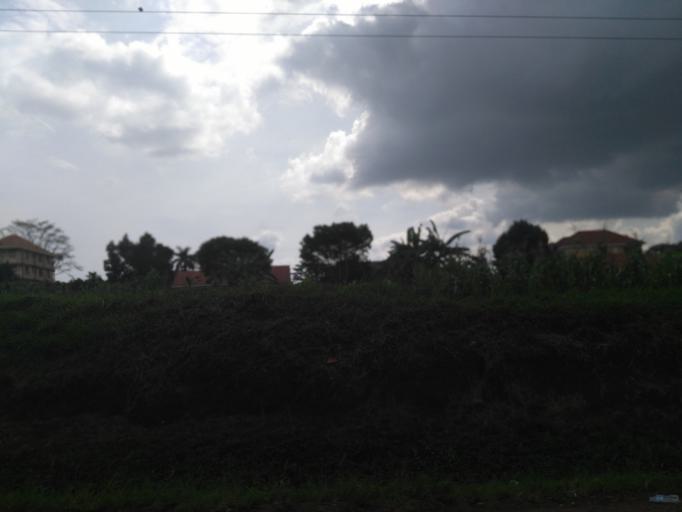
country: UG
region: Eastern Region
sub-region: Jinja District
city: Jinja
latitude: 0.4437
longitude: 33.2069
